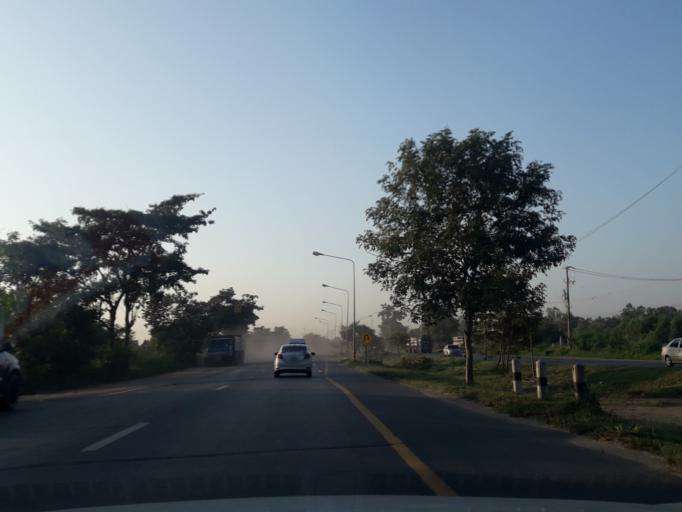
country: TH
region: Phra Nakhon Si Ayutthaya
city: Bang Pa-in
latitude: 14.2471
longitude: 100.5367
